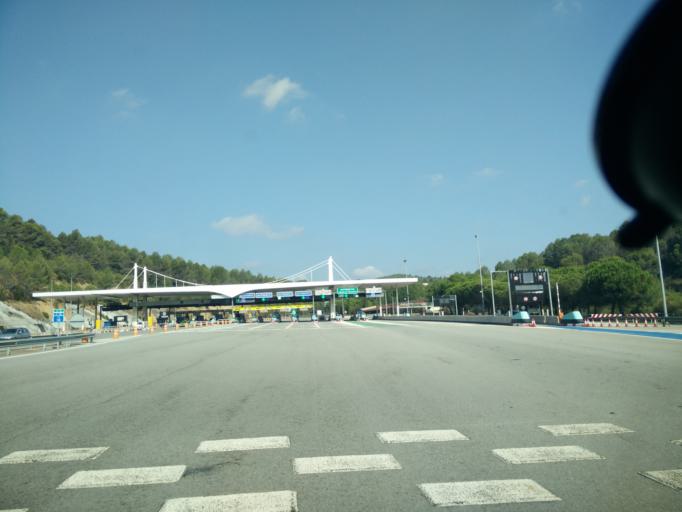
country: ES
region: Catalonia
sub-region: Provincia de Barcelona
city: Rubi
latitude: 41.5174
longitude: 2.0317
